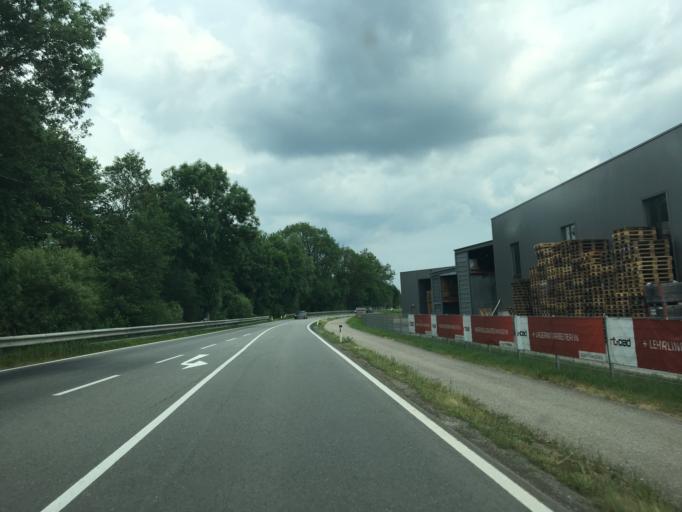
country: AT
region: Upper Austria
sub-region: Politischer Bezirk Braunau am Inn
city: Braunau am Inn
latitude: 48.1451
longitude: 13.1313
